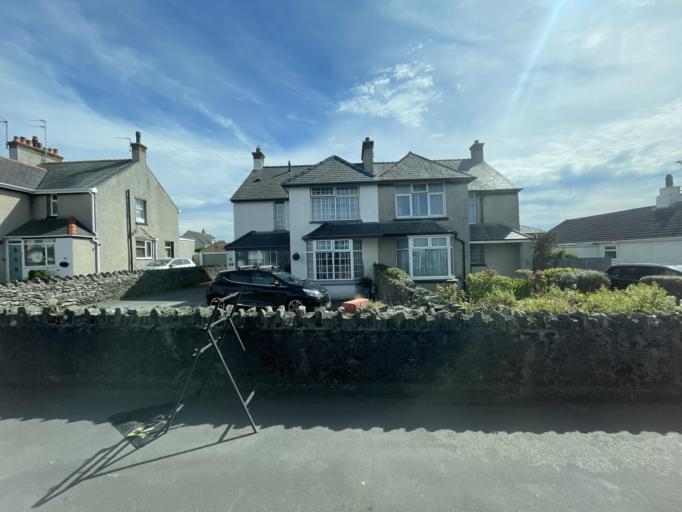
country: GB
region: Wales
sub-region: Anglesey
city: Holyhead
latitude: 53.3036
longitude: -4.6227
